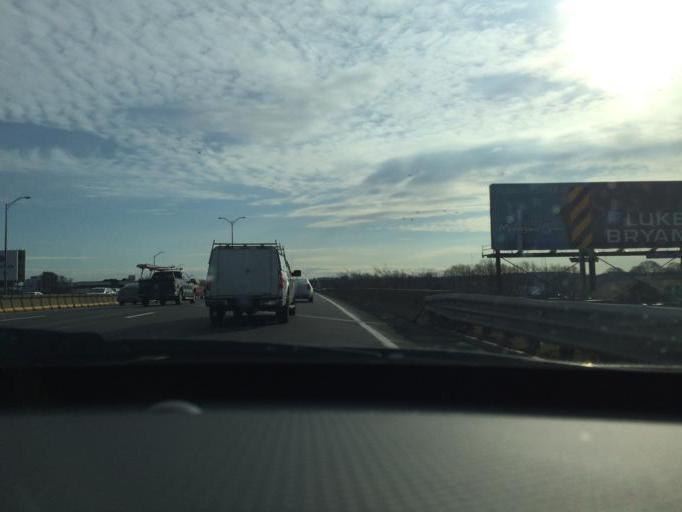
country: US
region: Massachusetts
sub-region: Suffolk County
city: South Boston
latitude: 42.2907
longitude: -71.0439
